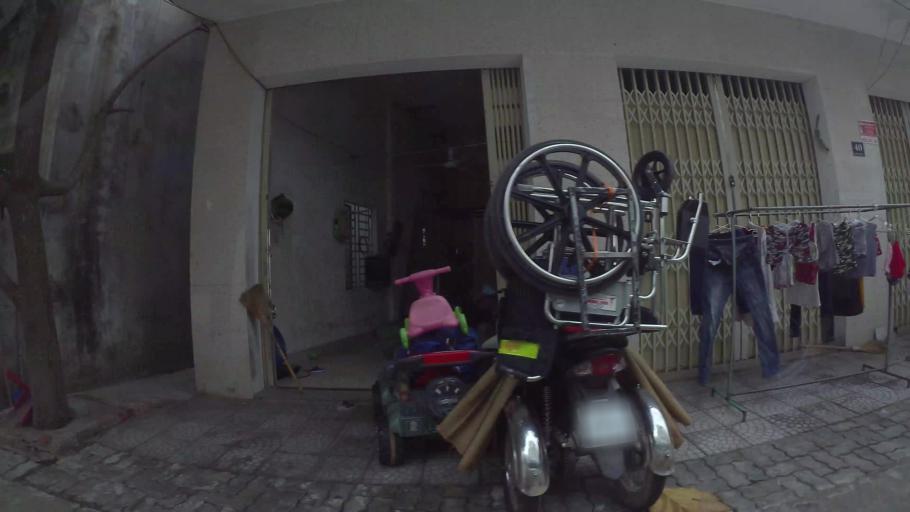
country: VN
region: Da Nang
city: Thanh Khe
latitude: 16.0677
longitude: 108.1905
